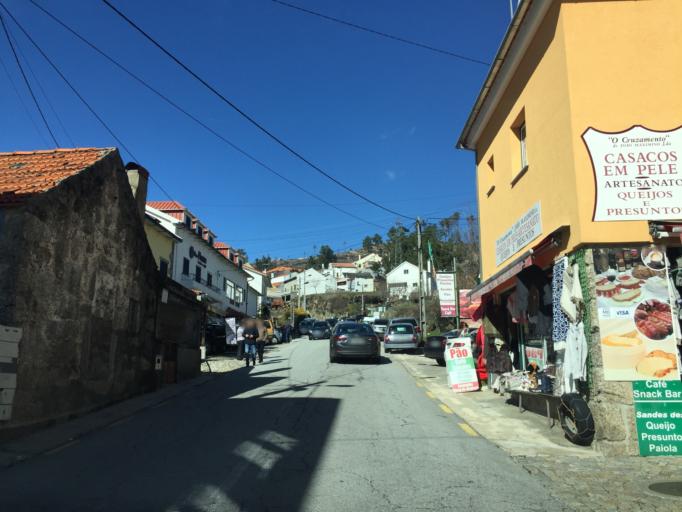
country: PT
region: Guarda
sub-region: Seia
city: Seia
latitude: 40.4022
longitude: -7.6414
